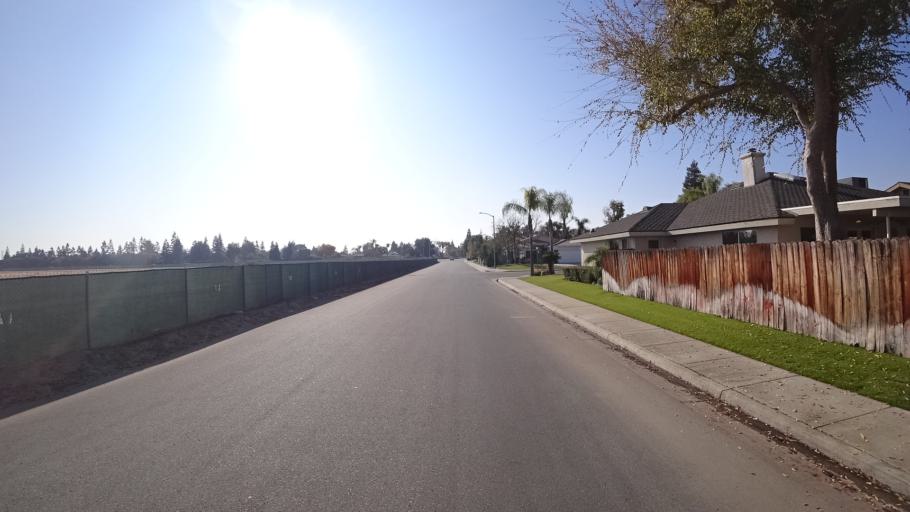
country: US
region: California
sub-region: Kern County
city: Greenacres
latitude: 35.3705
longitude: -119.1056
